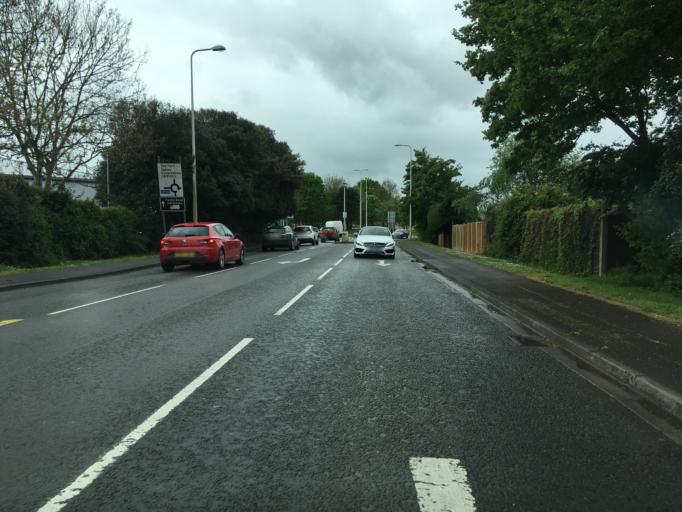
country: GB
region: England
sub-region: North Somerset
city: Clevedon
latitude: 51.4343
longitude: -2.8432
